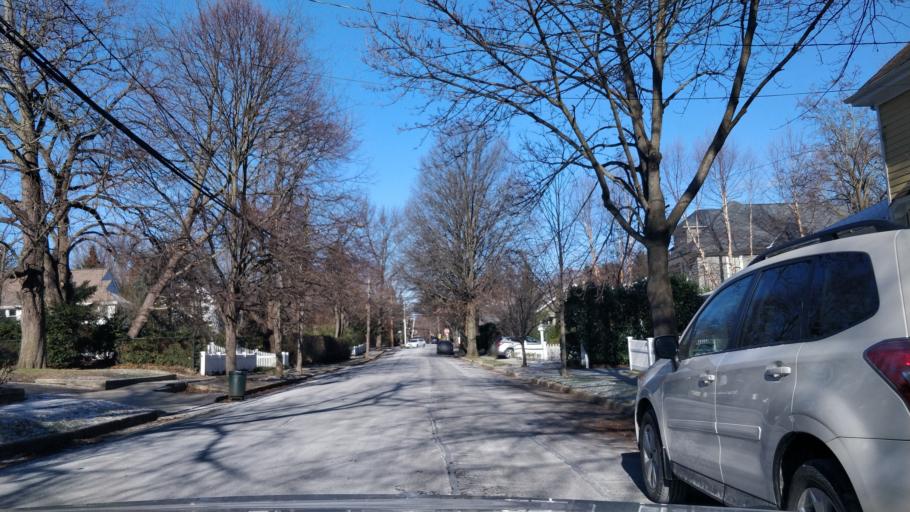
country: US
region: New York
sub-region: Nassau County
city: Sea Cliff
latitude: 40.8493
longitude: -73.6416
